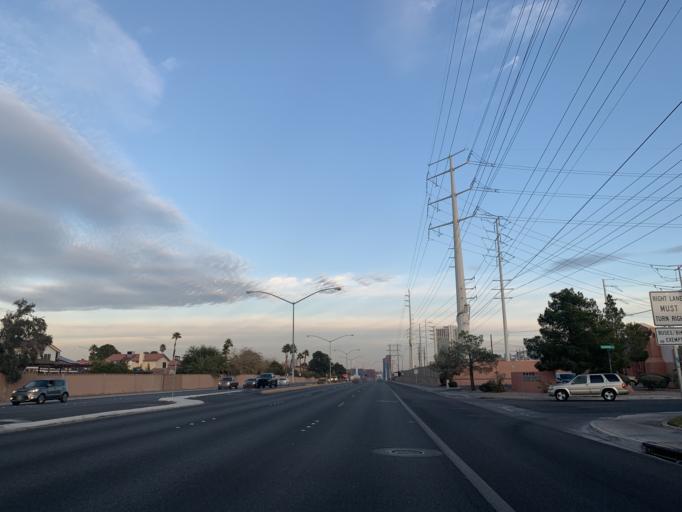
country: US
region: Nevada
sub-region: Clark County
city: Spring Valley
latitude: 36.1149
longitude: -115.2153
